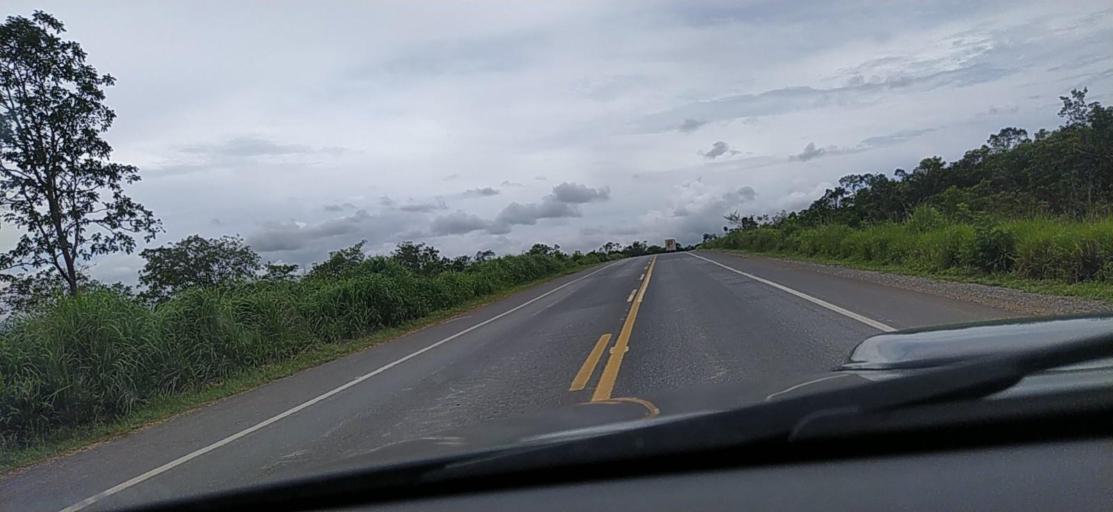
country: BR
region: Minas Gerais
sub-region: Corinto
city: Corinto
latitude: -18.3006
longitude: -44.4110
